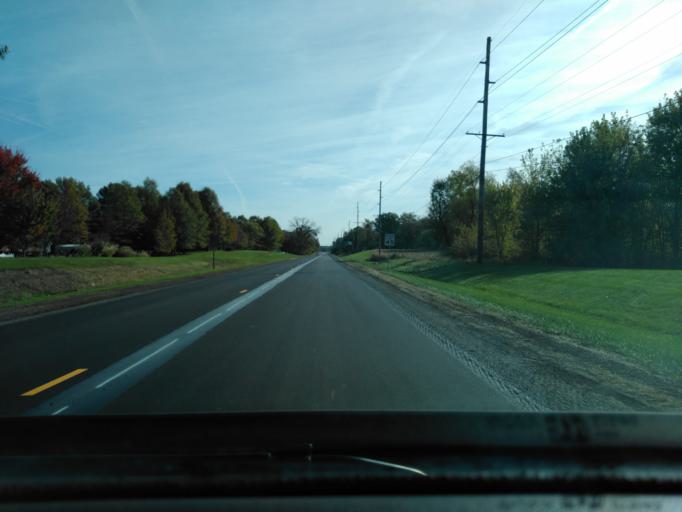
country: US
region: Illinois
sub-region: Madison County
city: Troy
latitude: 38.7177
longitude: -89.8654
